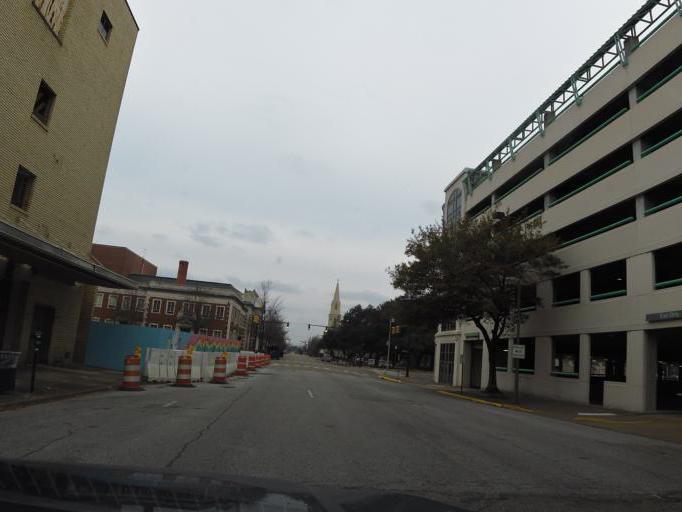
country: US
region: Alabama
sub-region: Montgomery County
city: Montgomery
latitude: 32.3780
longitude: -86.3075
